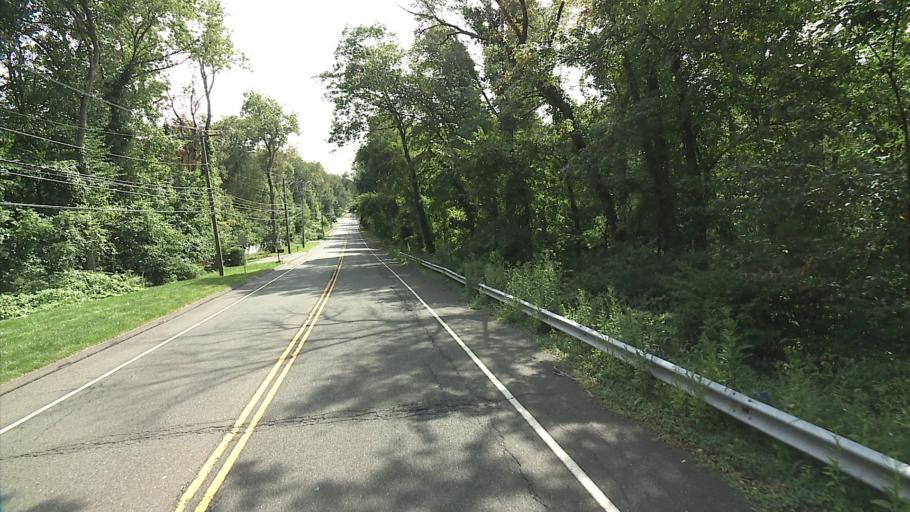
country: US
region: Connecticut
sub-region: Fairfield County
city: North Stamford
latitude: 41.1589
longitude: -73.5604
